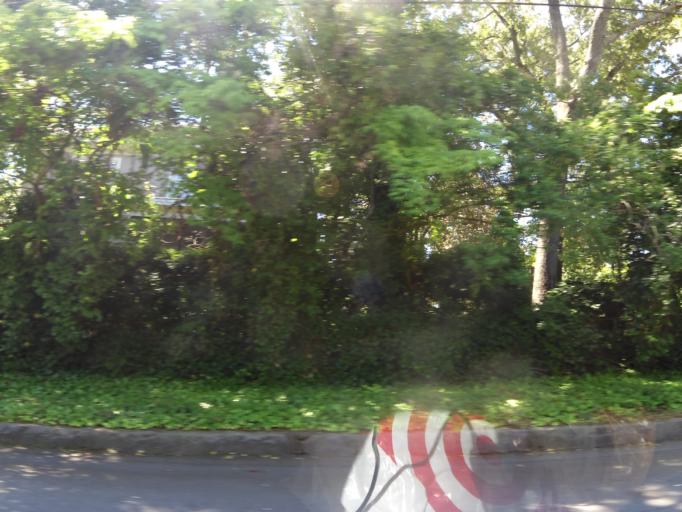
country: US
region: Georgia
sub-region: Richmond County
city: Augusta
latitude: 33.4803
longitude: -82.0267
